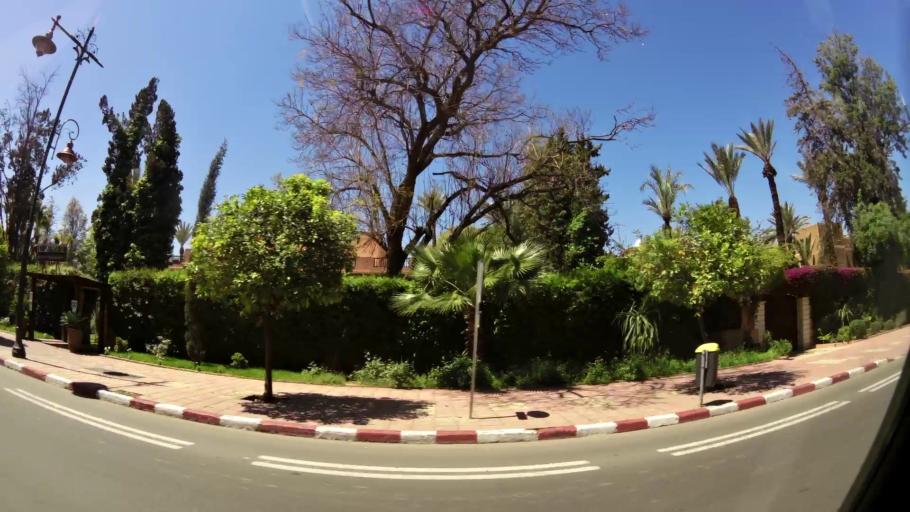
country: MA
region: Marrakech-Tensift-Al Haouz
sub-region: Marrakech
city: Marrakesh
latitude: 31.6257
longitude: -8.0013
